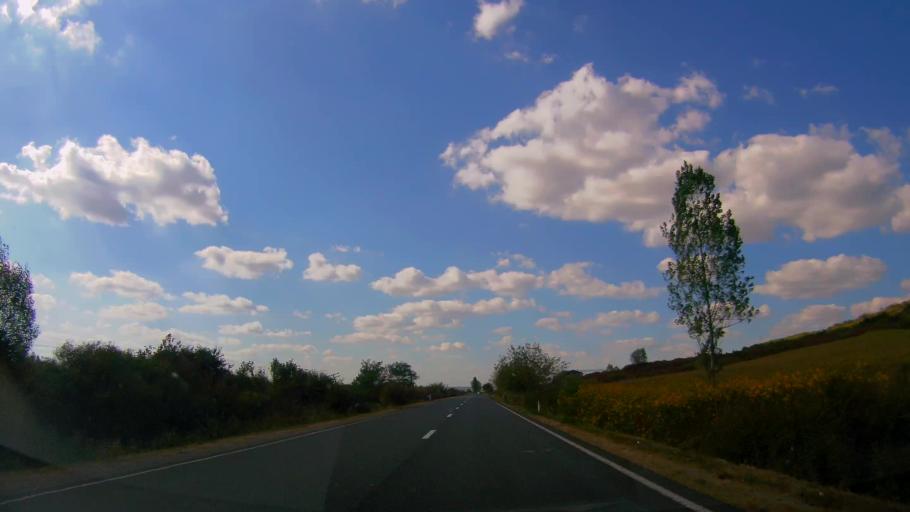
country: RO
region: Salaj
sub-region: Comuna Sarmasag
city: Sarmasag
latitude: 47.3292
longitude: 22.8645
